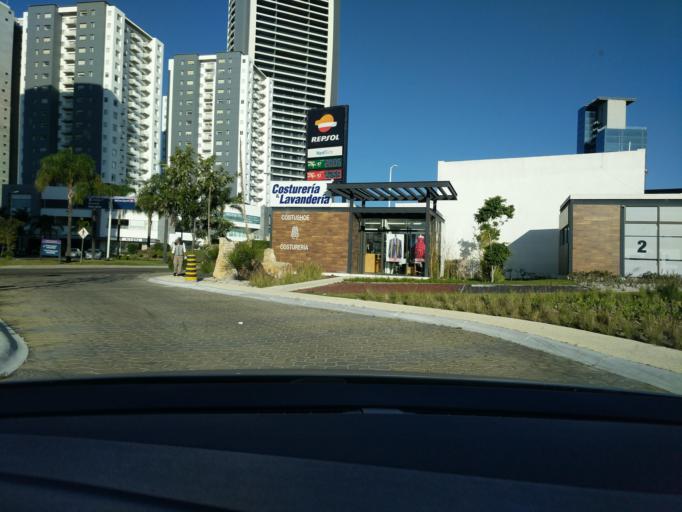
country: MX
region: Puebla
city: Santa Clara
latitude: 18.9954
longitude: -98.2774
